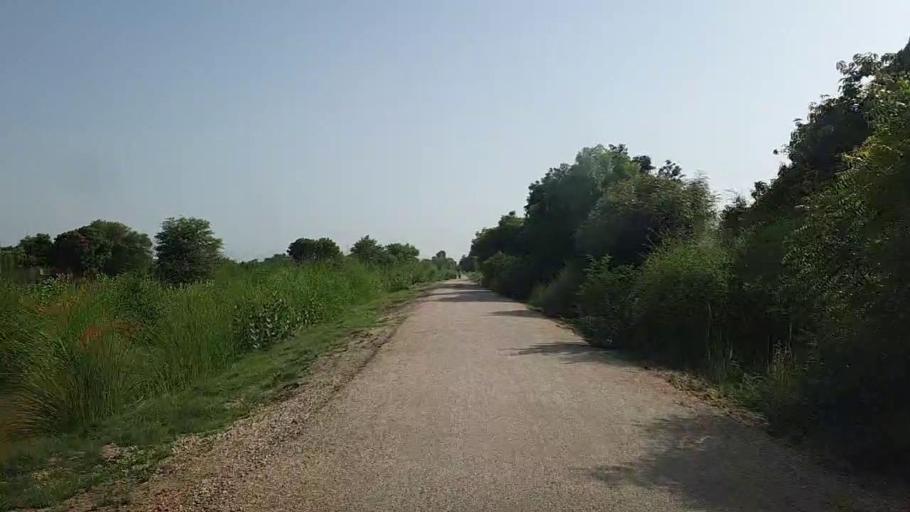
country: PK
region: Sindh
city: Karaundi
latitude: 26.8616
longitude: 68.3660
